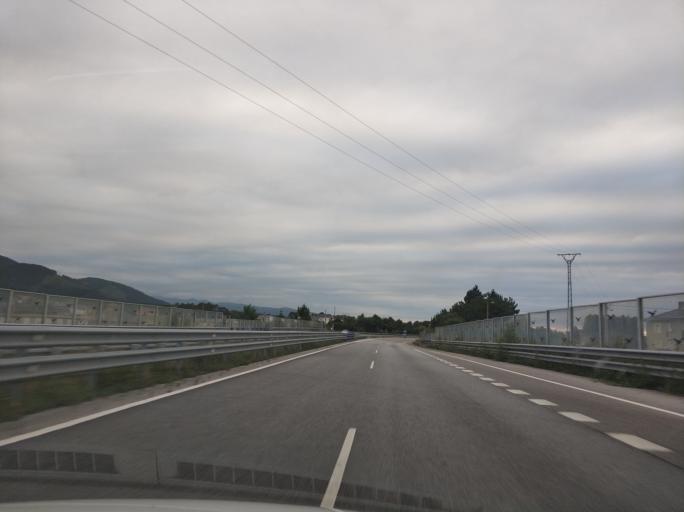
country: ES
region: Asturias
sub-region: Province of Asturias
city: Tineo
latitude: 43.5461
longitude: -6.4524
